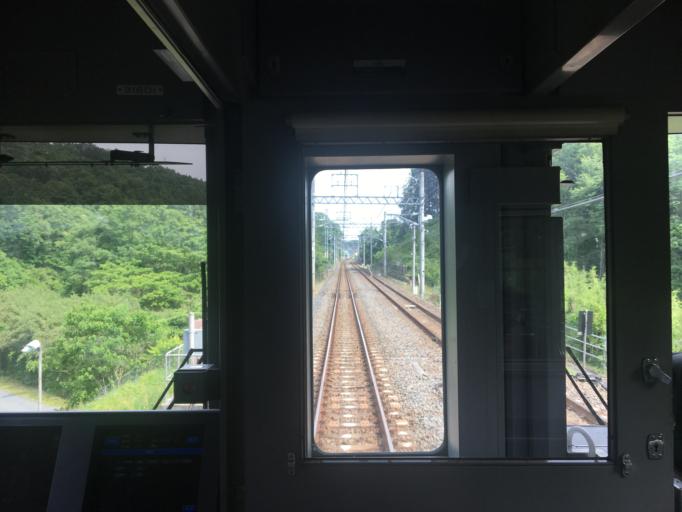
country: JP
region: Saitama
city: Ogawa
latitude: 36.0553
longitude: 139.3012
